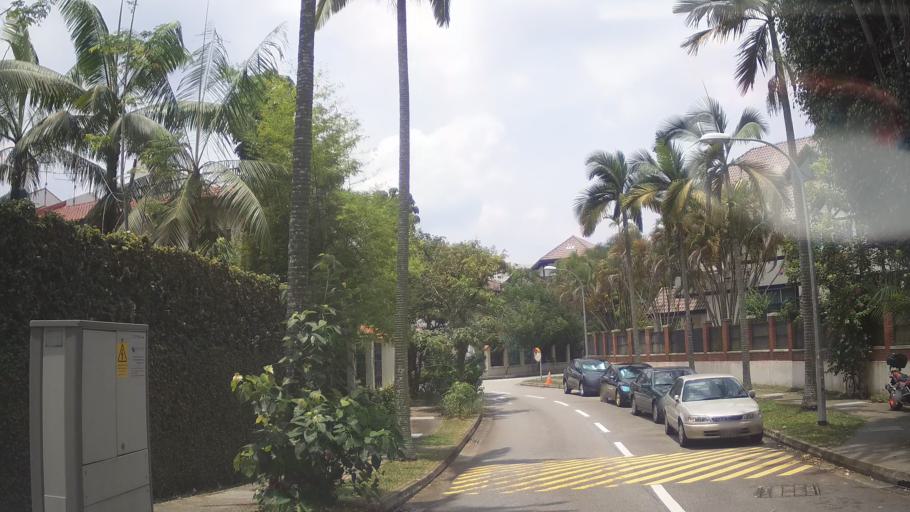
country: MY
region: Johor
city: Johor Bahru
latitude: 1.3704
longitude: 103.7702
